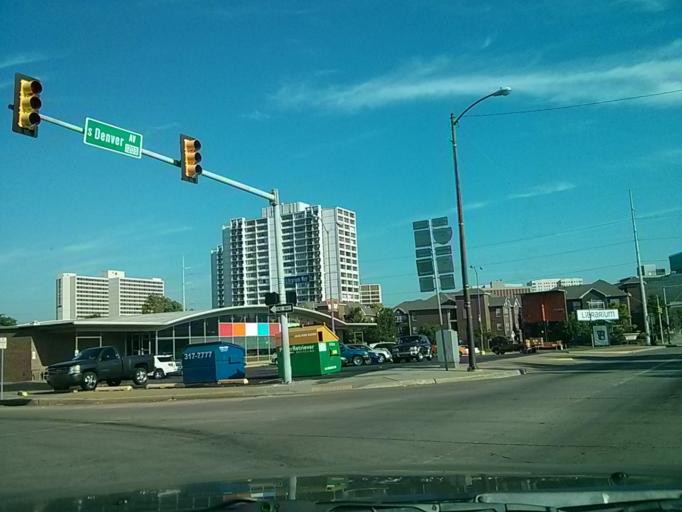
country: US
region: Oklahoma
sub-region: Tulsa County
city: Tulsa
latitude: 36.1449
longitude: -95.9924
